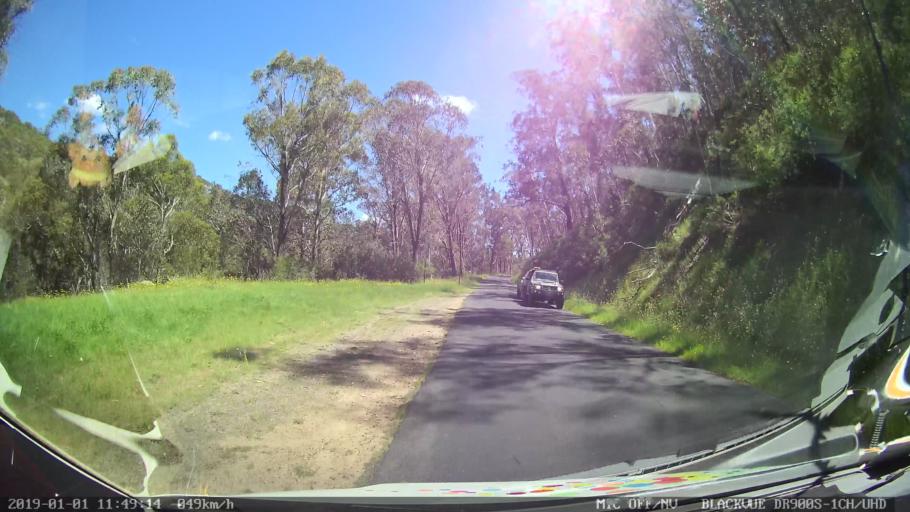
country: AU
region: New South Wales
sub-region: Snowy River
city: Jindabyne
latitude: -35.8953
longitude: 148.4138
